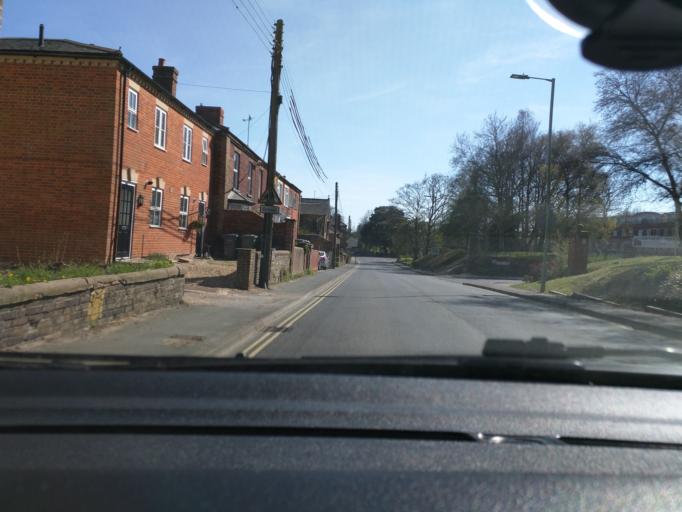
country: GB
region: England
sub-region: Suffolk
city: Leiston
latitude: 52.2091
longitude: 1.5746
